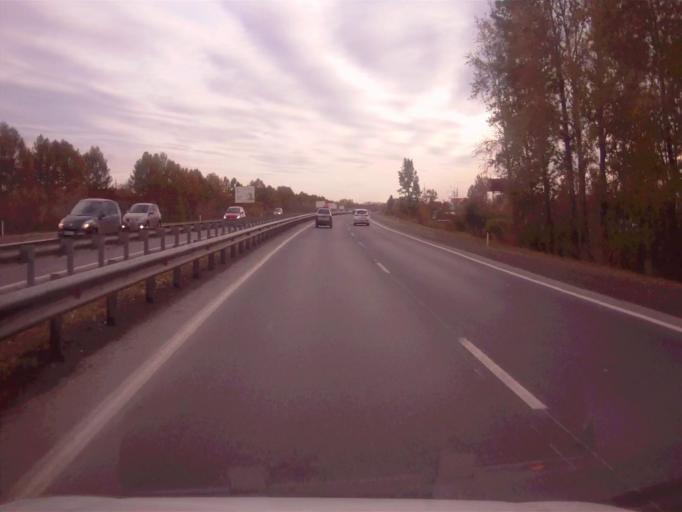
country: RU
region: Chelyabinsk
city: Novosineglazovskiy
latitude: 55.0273
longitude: 61.4496
